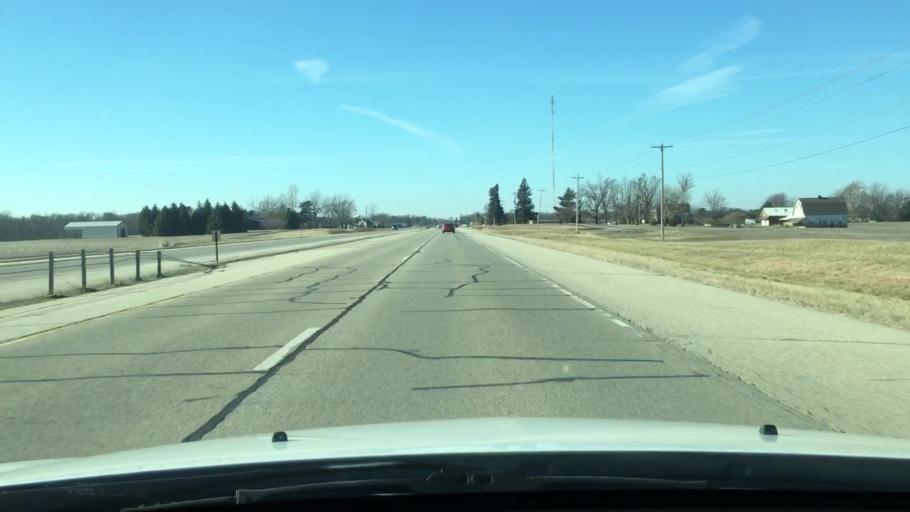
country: US
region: Illinois
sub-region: Woodford County
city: Germantown Hills
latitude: 40.7732
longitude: -89.4357
